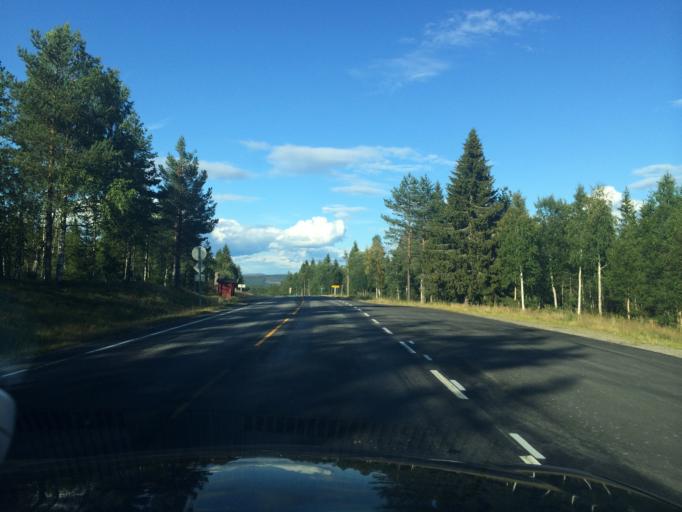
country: NO
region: Hedmark
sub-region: Valer
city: Valer
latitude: 61.0503
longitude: 11.9350
